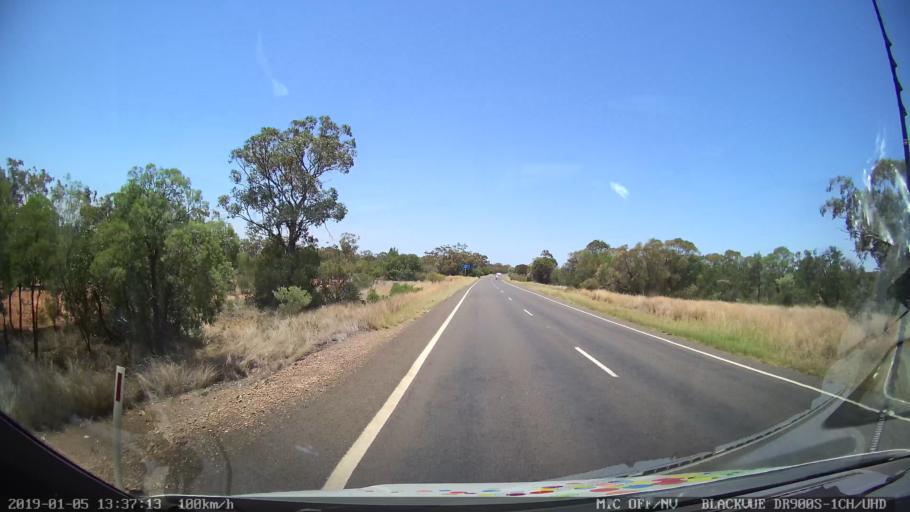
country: AU
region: New South Wales
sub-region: Gunnedah
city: Gunnedah
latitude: -30.9819
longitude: 150.1777
